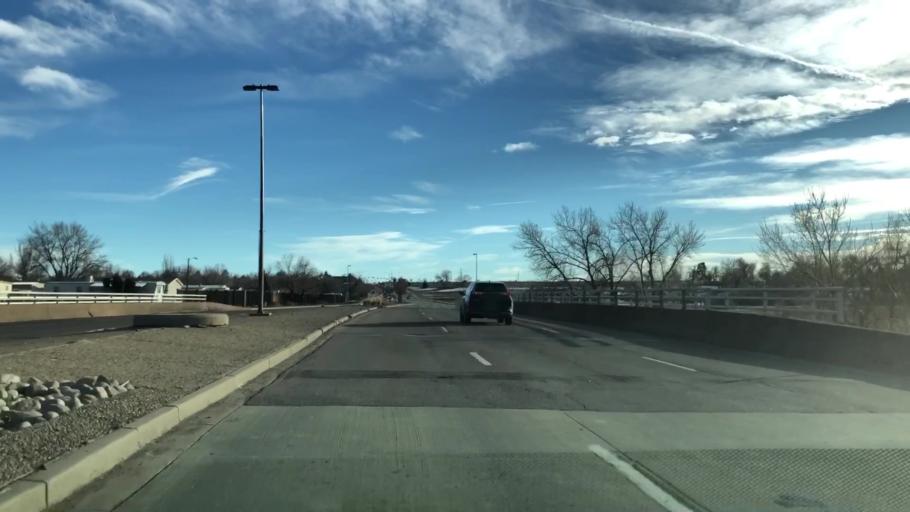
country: US
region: Colorado
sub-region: Adams County
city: Aurora
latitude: 39.7484
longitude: -104.7913
